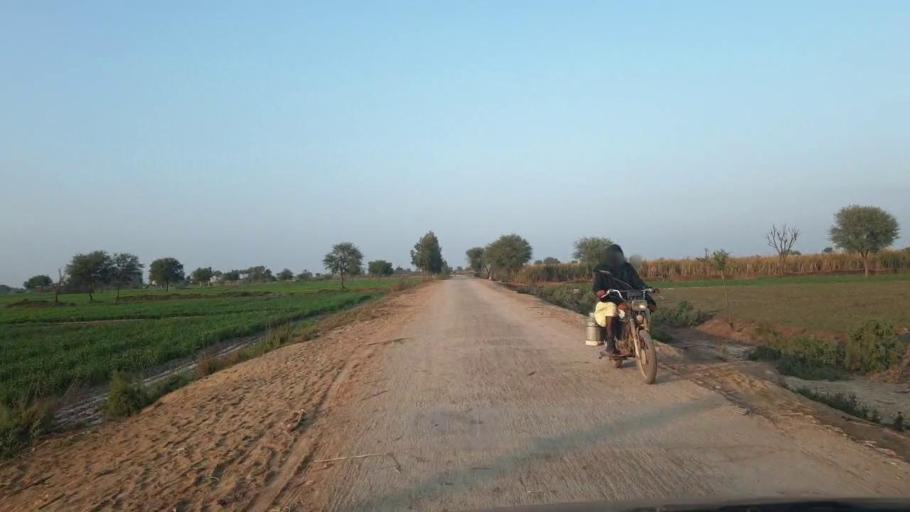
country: PK
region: Sindh
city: Berani
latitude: 25.8452
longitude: 68.7516
